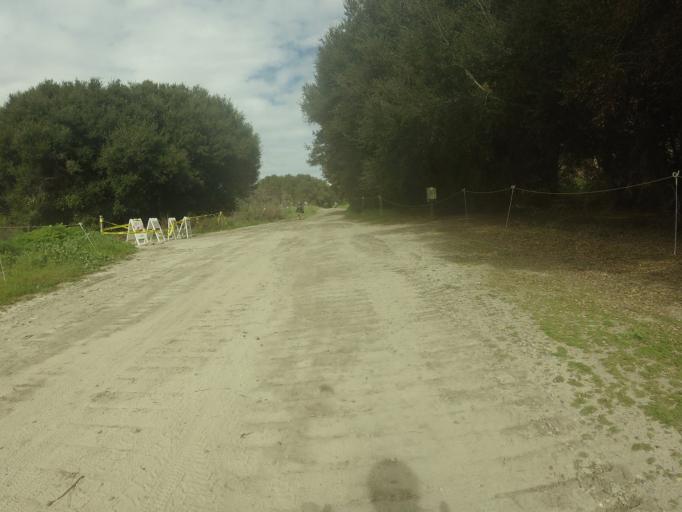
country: US
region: California
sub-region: Orange County
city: Aliso Viejo
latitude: 33.5549
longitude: -117.7411
